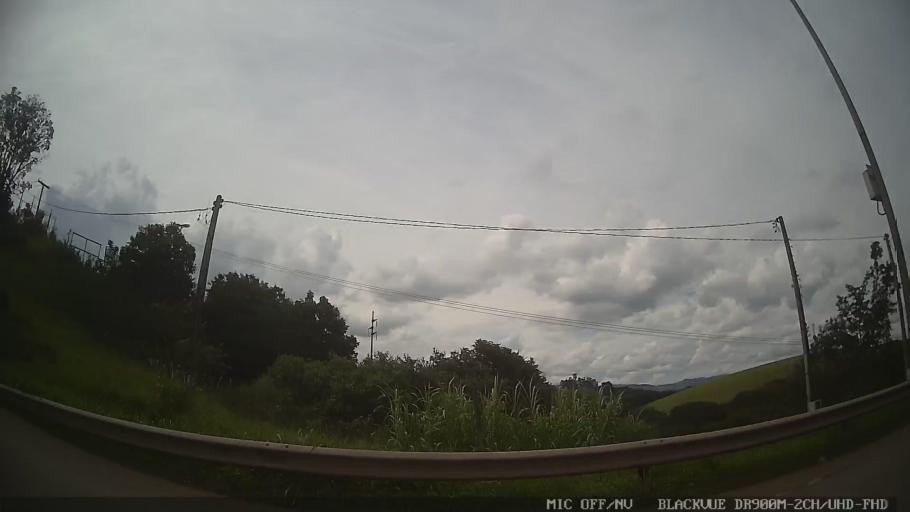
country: BR
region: Minas Gerais
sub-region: Extrema
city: Extrema
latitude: -22.8231
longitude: -46.3076
